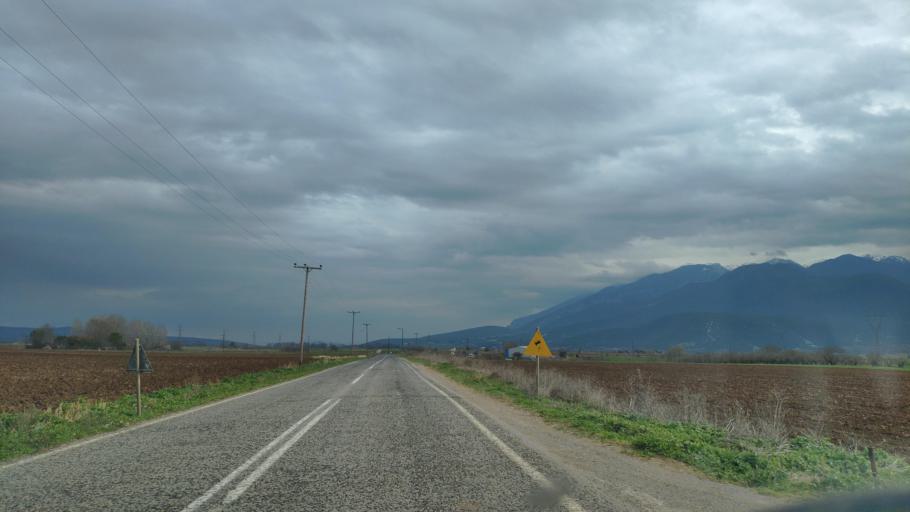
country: GR
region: Central Greece
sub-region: Nomos Fthiotidos
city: Amfikleia
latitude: 38.6951
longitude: 22.5243
